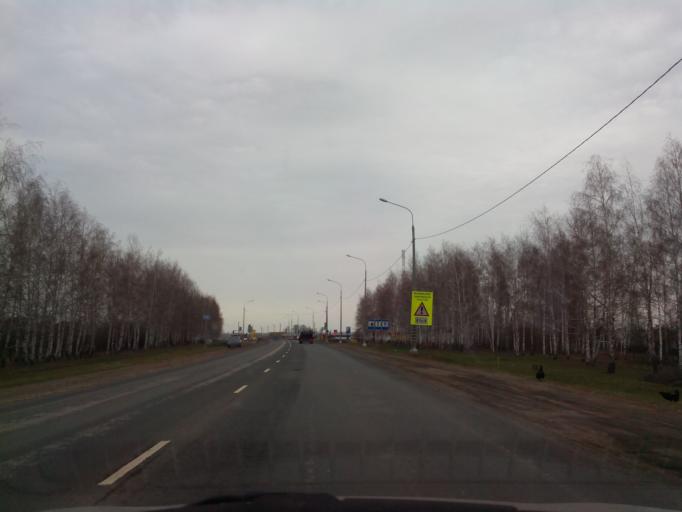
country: RU
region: Tambov
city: Zavoronezhskoye
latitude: 52.9726
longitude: 40.5703
